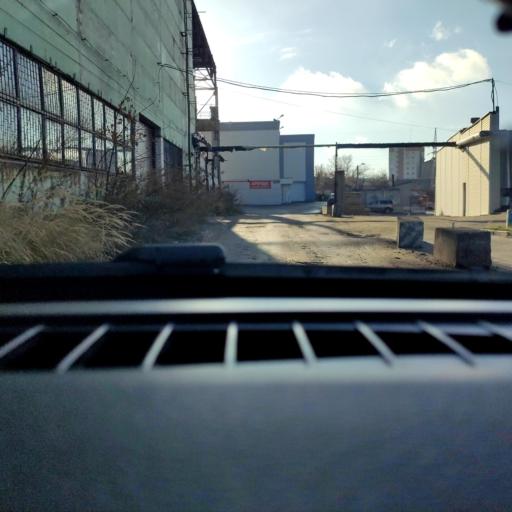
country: RU
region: Voronezj
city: Voronezh
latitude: 51.6634
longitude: 39.1764
